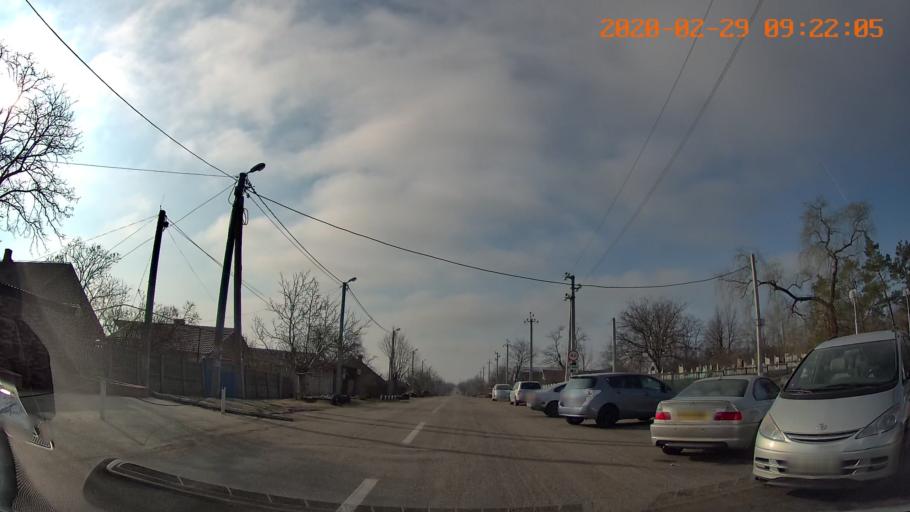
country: MD
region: Telenesti
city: Pervomaisc
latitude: 46.7379
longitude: 29.9651
